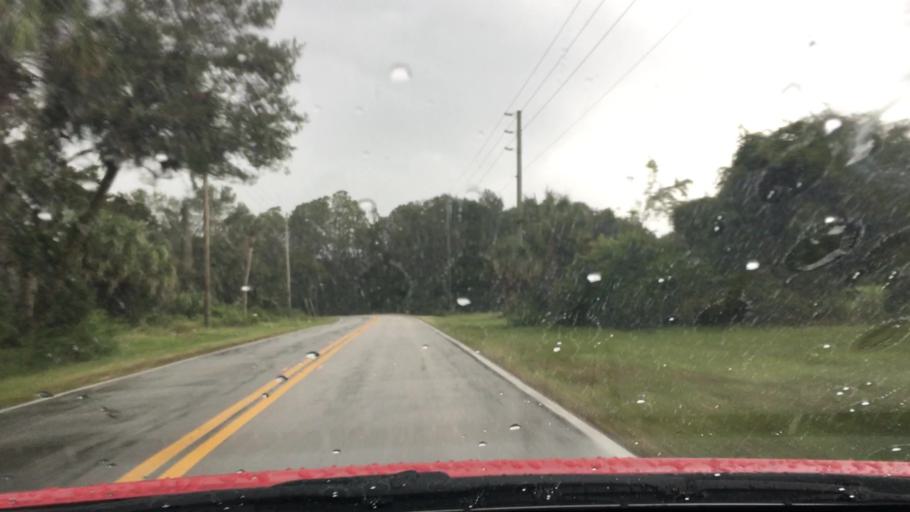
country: US
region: Florida
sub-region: Pasco County
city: Land O' Lakes
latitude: 28.2674
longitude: -82.4460
